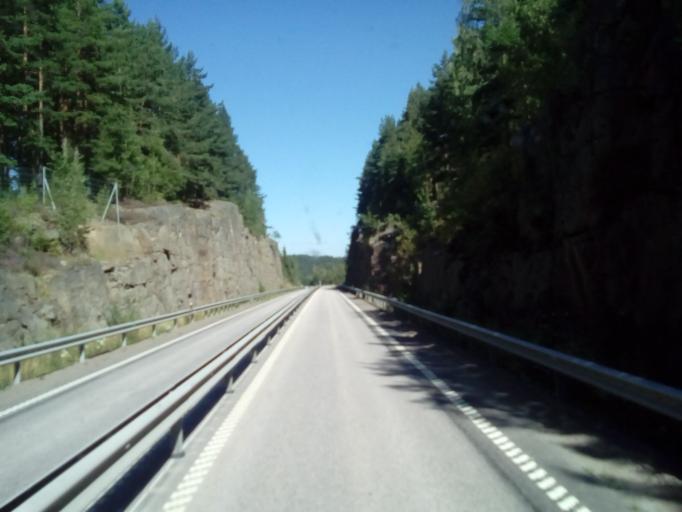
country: SE
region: OEstergoetland
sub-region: Kinda Kommun
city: Rimforsa
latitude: 58.0968
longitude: 15.6639
